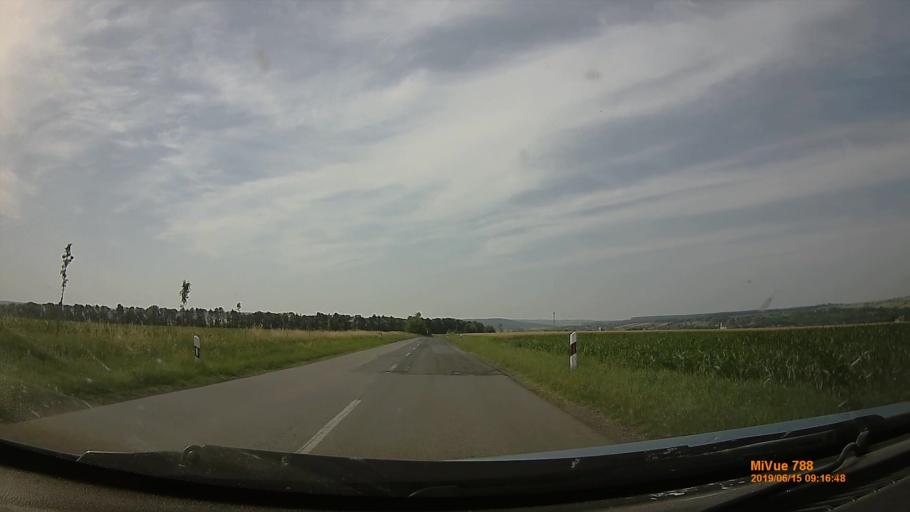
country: HU
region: Tolna
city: Tamasi
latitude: 46.6109
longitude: 18.2067
